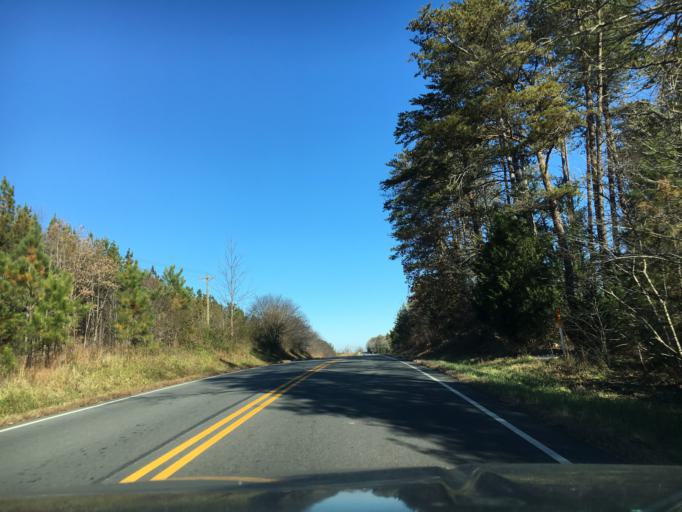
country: US
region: Virginia
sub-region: Buckingham County
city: Buckingham
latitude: 37.5235
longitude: -78.6170
